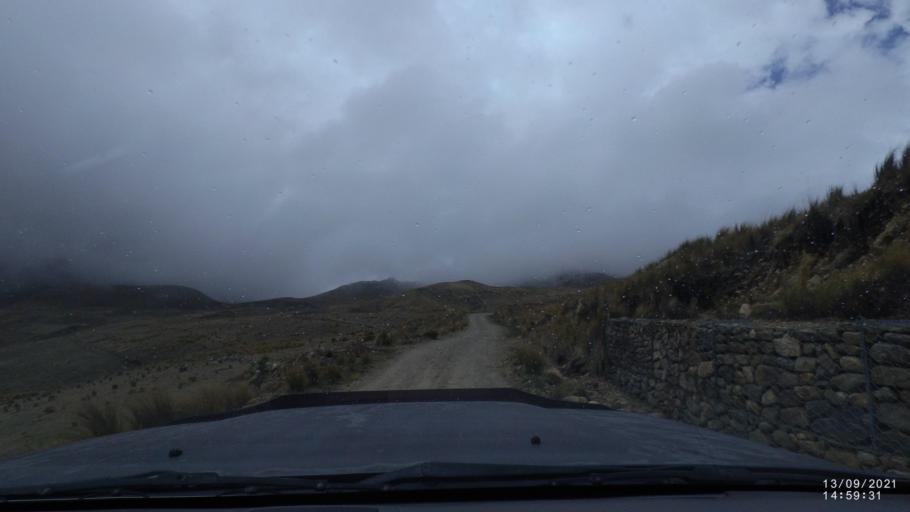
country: BO
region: Cochabamba
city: Colomi
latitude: -17.3312
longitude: -65.7877
